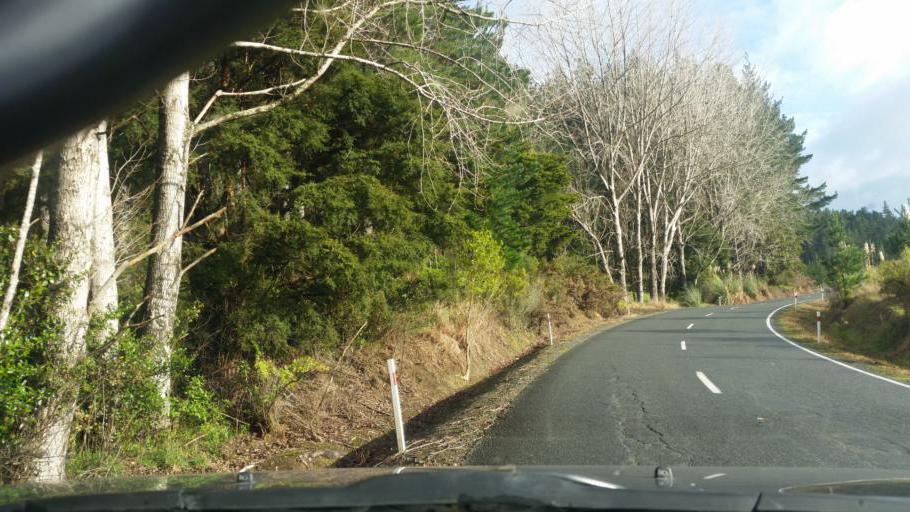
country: NZ
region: Northland
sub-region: Kaipara District
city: Dargaville
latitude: -35.7394
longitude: 173.8704
